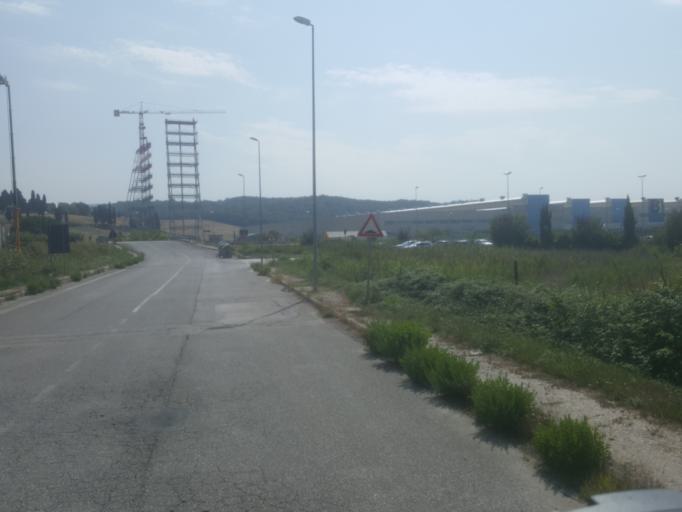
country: IT
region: Tuscany
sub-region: Provincia di Livorno
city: Guasticce
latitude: 43.5965
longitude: 10.4007
